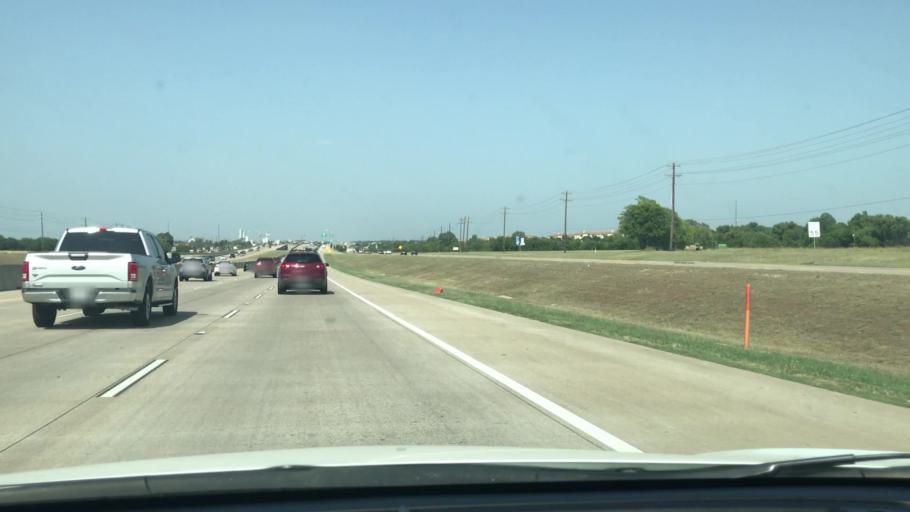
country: US
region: Texas
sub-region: Collin County
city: Frisco
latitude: 33.1152
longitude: -96.7588
